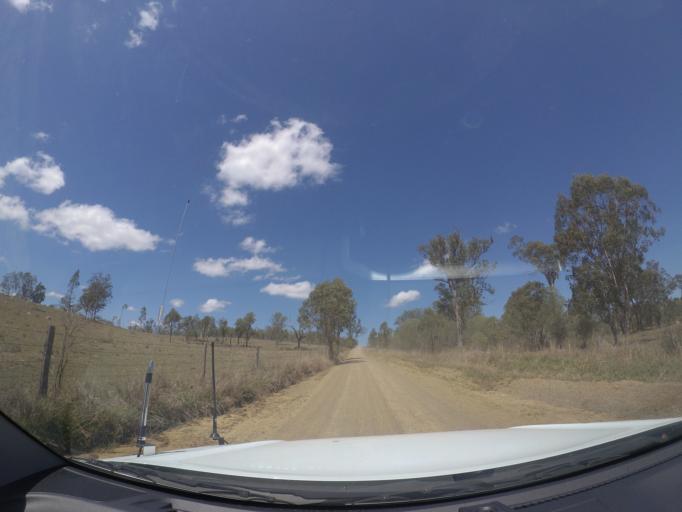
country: AU
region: Queensland
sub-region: Logan
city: Cedar Vale
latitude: -27.8534
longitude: 152.8862
